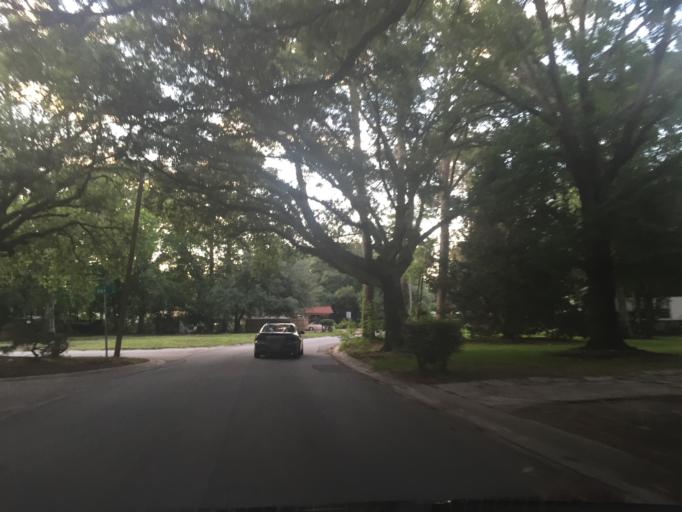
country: US
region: Georgia
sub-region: Chatham County
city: Montgomery
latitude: 31.9937
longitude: -81.1251
